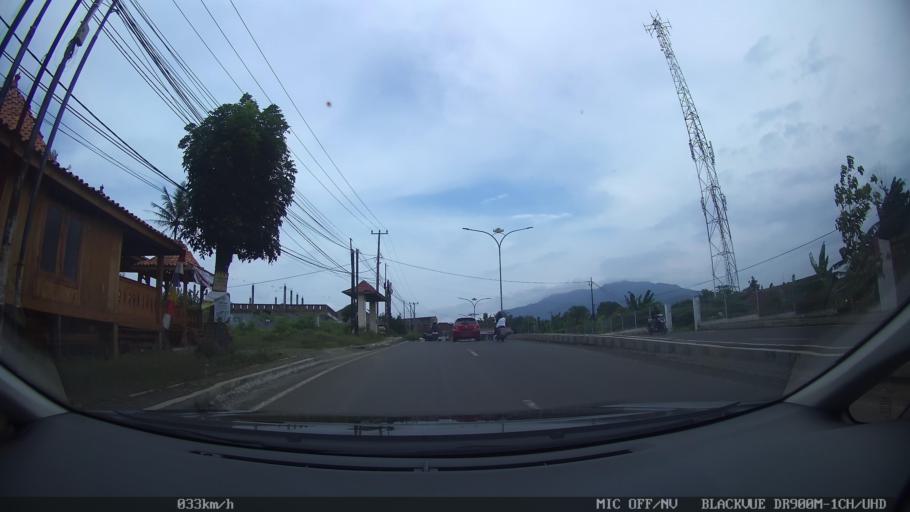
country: ID
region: Lampung
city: Kedaton
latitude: -5.3894
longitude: 105.2199
